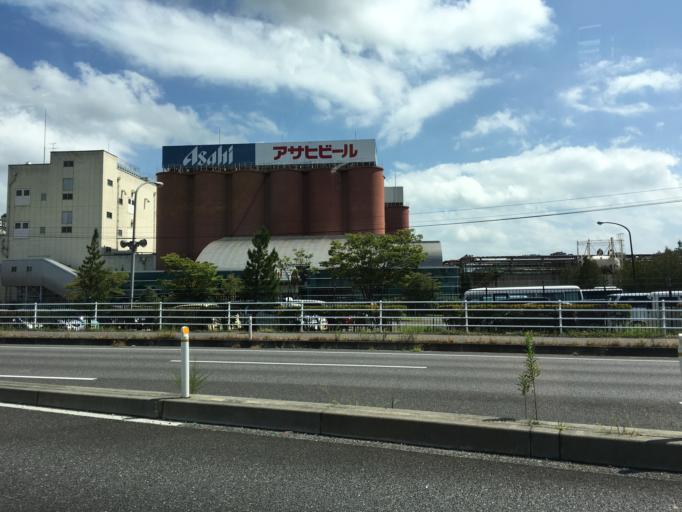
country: JP
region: Fukushima
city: Motomiya
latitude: 37.4787
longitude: 140.3790
